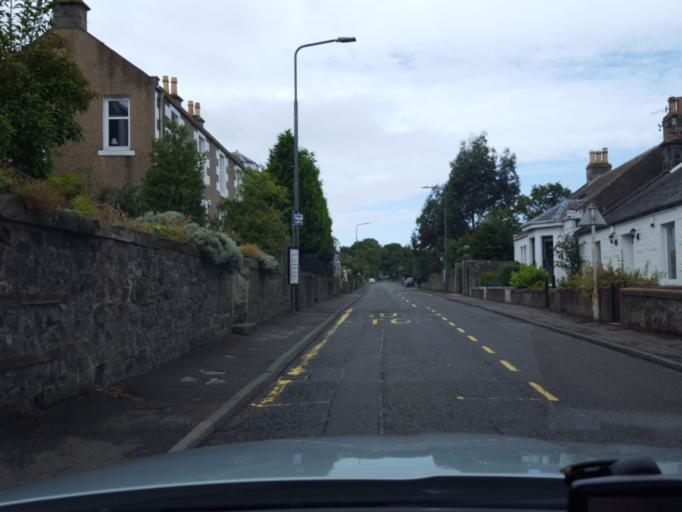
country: GB
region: Scotland
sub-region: Fife
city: Tayport
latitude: 56.4515
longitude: -2.8864
